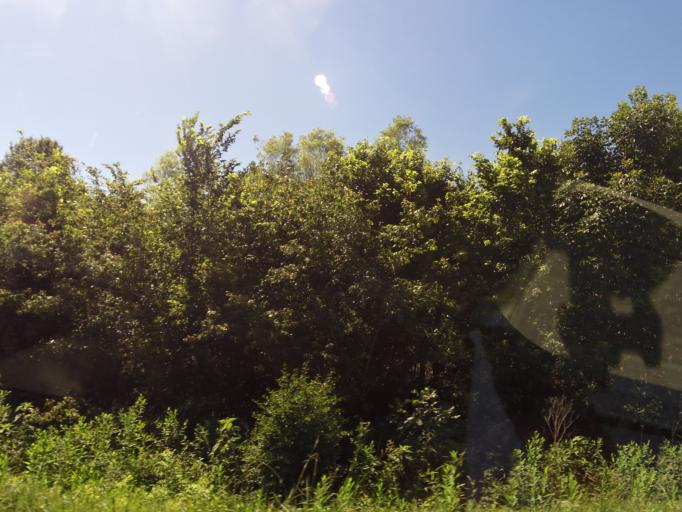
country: US
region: Missouri
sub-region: Dunklin County
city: Campbell
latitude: 36.4710
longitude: -90.1117
